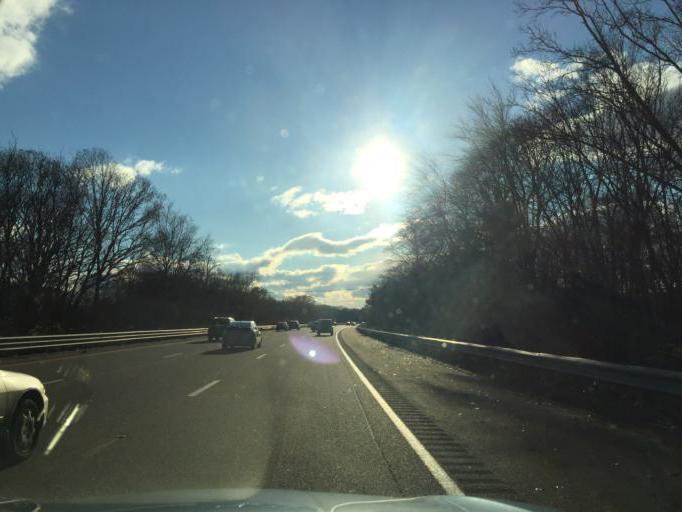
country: US
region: Massachusetts
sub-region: Bristol County
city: North Seekonk
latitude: 41.9091
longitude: -71.3413
